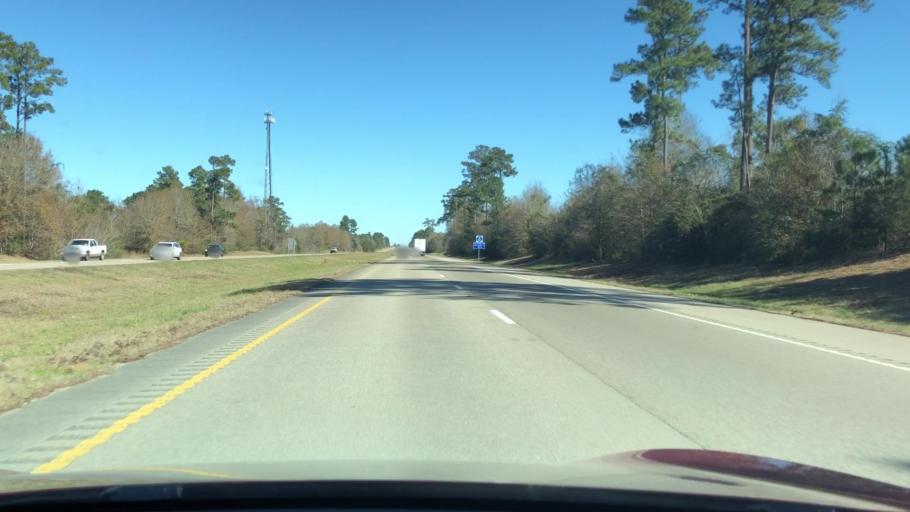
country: US
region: Mississippi
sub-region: Pearl River County
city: Poplarville
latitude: 30.7301
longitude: -89.5461
